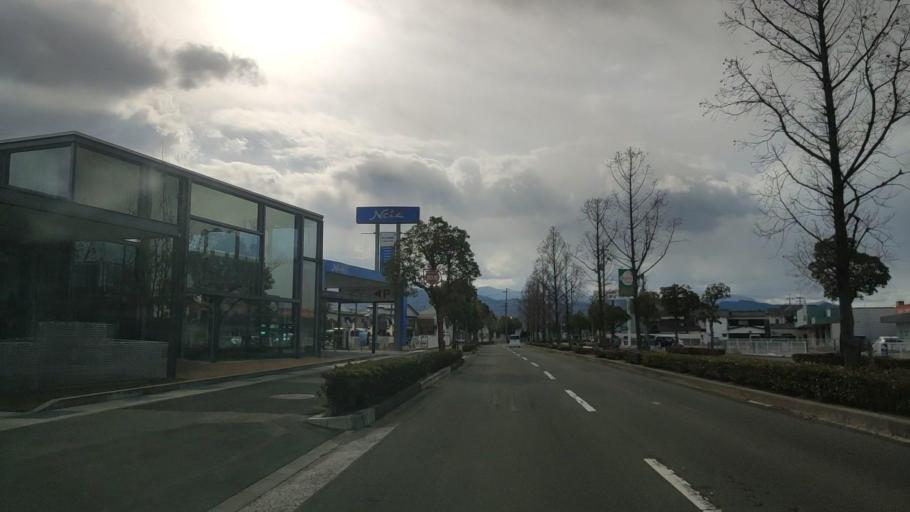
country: JP
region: Ehime
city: Saijo
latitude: 34.0511
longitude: 133.0118
